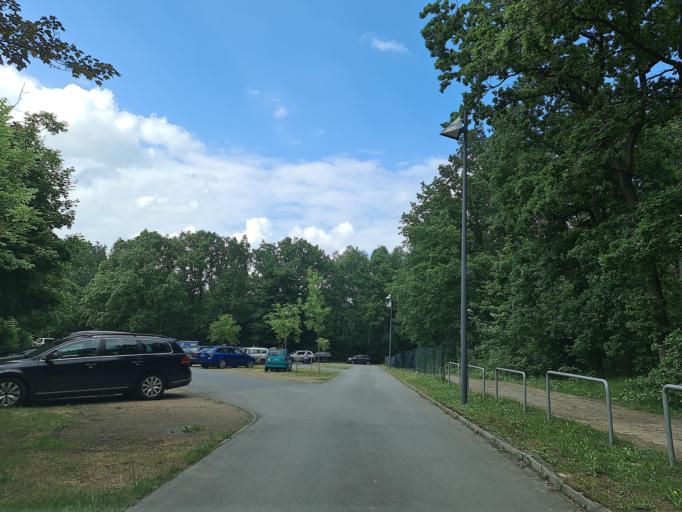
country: DE
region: Saxony
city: Pohl
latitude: 50.5405
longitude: 12.1853
